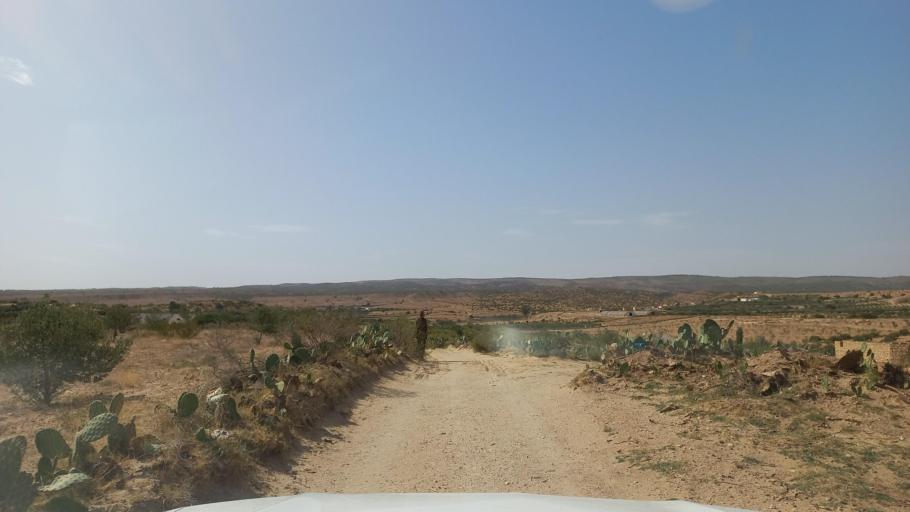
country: TN
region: Al Qasrayn
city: Kasserine
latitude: 35.2991
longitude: 8.9483
